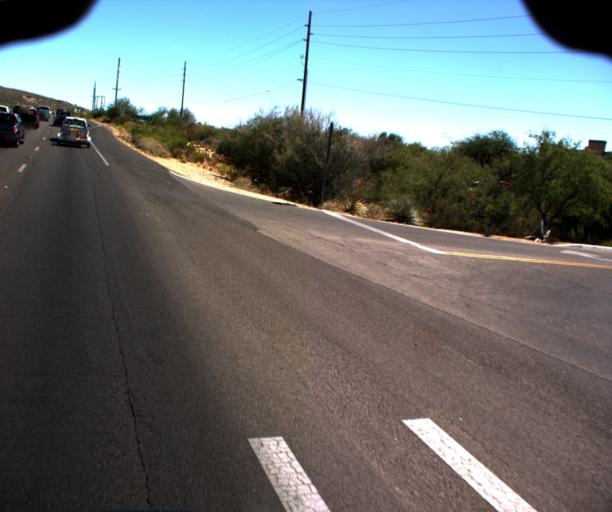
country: US
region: Arizona
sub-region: Pima County
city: Oro Valley
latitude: 32.3865
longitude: -110.9645
